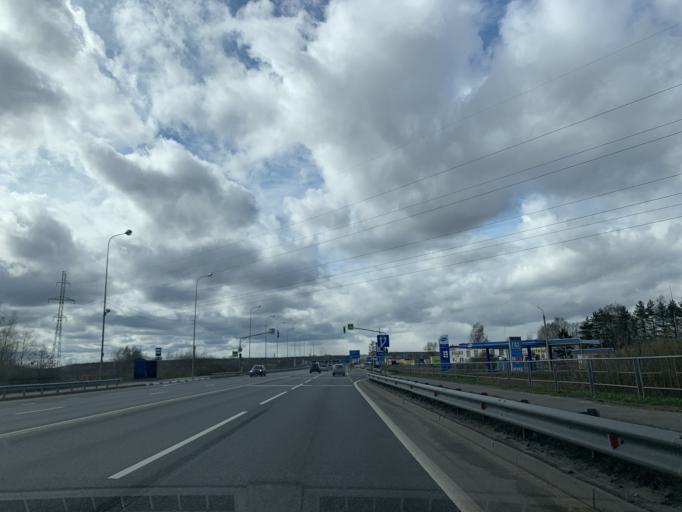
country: RU
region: Jaroslavl
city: Yaroslavl
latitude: 57.6836
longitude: 39.9124
